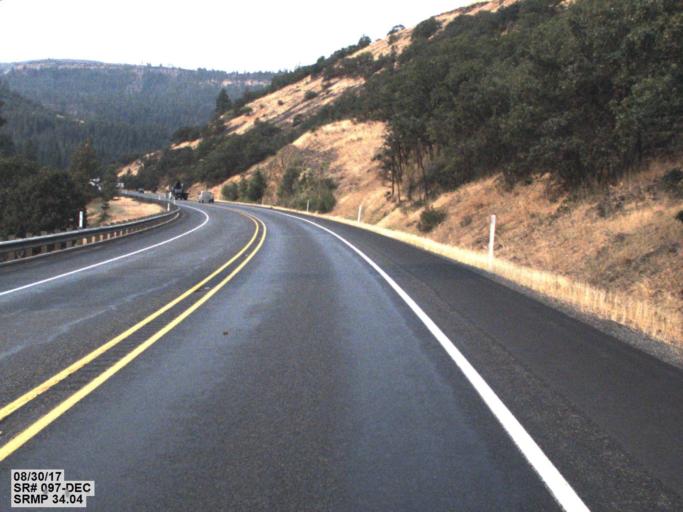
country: US
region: Washington
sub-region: Klickitat County
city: Goldendale
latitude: 46.0486
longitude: -120.5704
